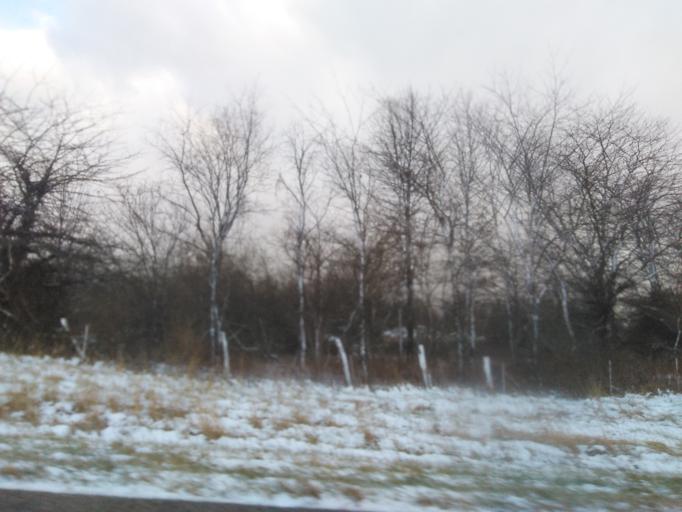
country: US
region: Illinois
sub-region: Madison County
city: Highland
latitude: 38.8259
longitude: -89.5534
